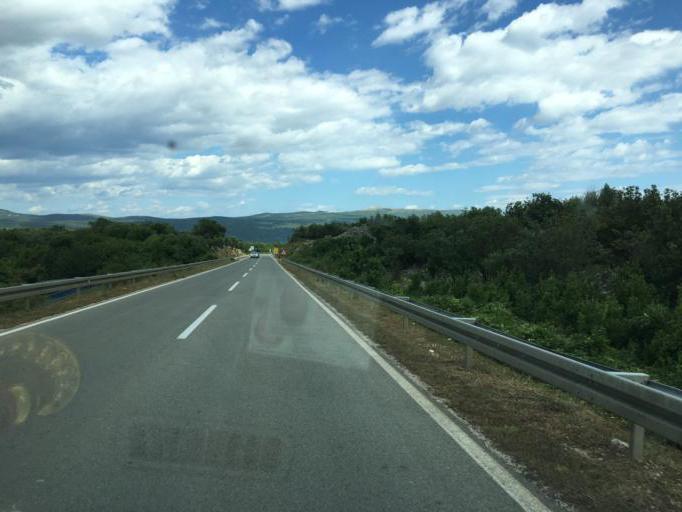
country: HR
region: Primorsko-Goranska
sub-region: Grad Krk
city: Krk
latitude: 45.0328
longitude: 14.5866
